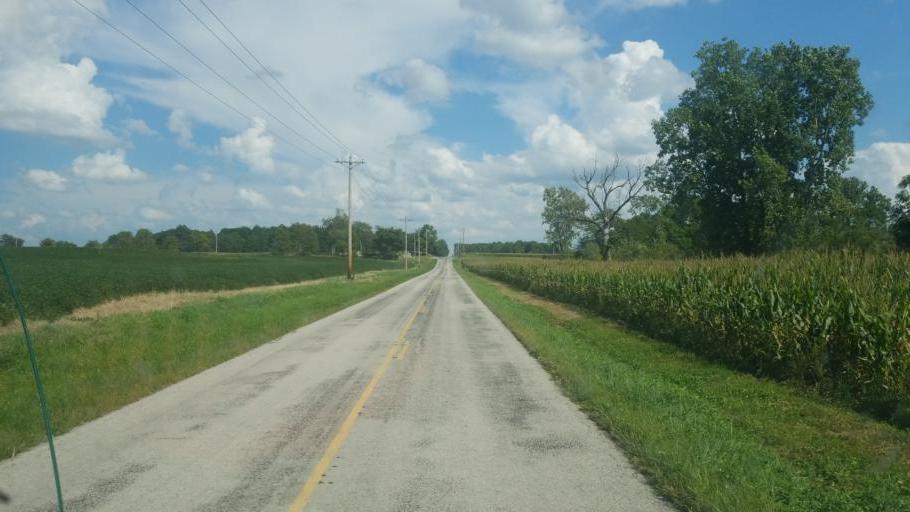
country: US
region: Ohio
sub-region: Seneca County
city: Tiffin
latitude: 40.9934
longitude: -83.1164
